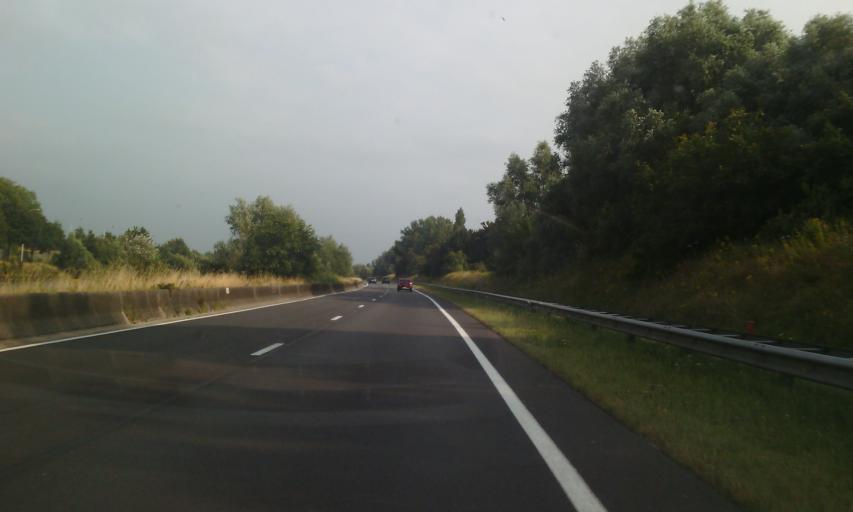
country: BE
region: Flanders
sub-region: Provincie Oost-Vlaanderen
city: Sint-Martens-Latem
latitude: 51.0624
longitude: 3.6602
